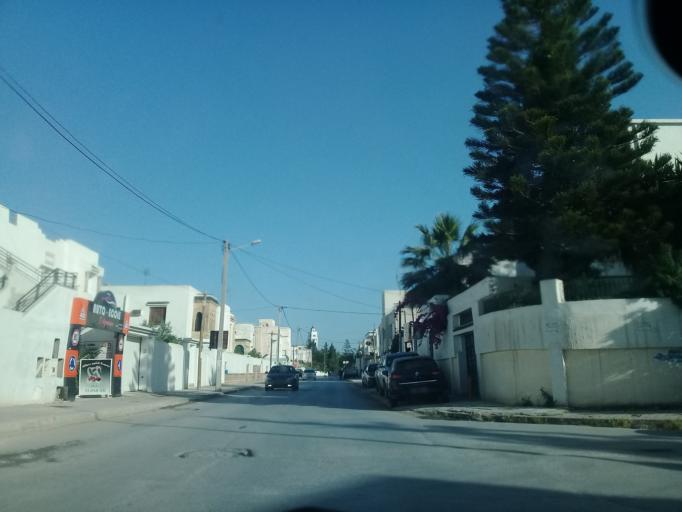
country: TN
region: Ariana
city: Ariana
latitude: 36.8377
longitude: 10.1965
